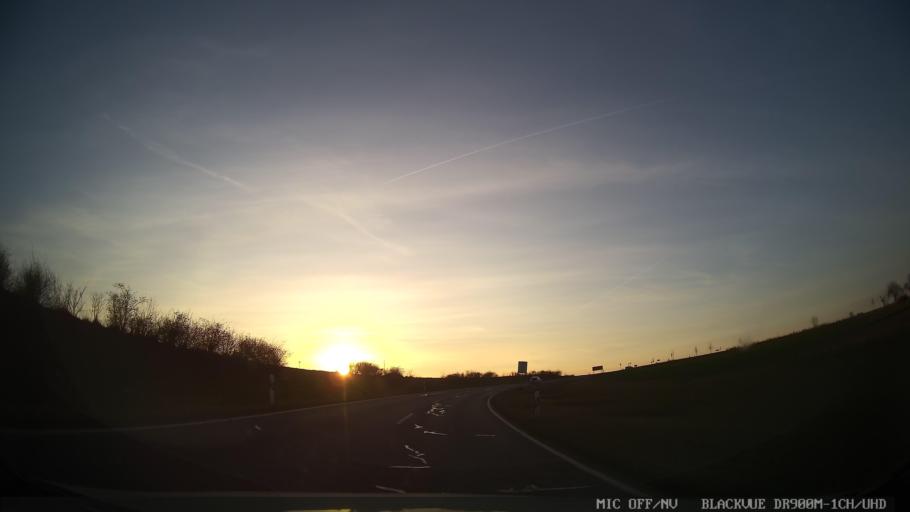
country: DE
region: Hesse
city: Reinheim
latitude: 49.8483
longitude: 8.8328
